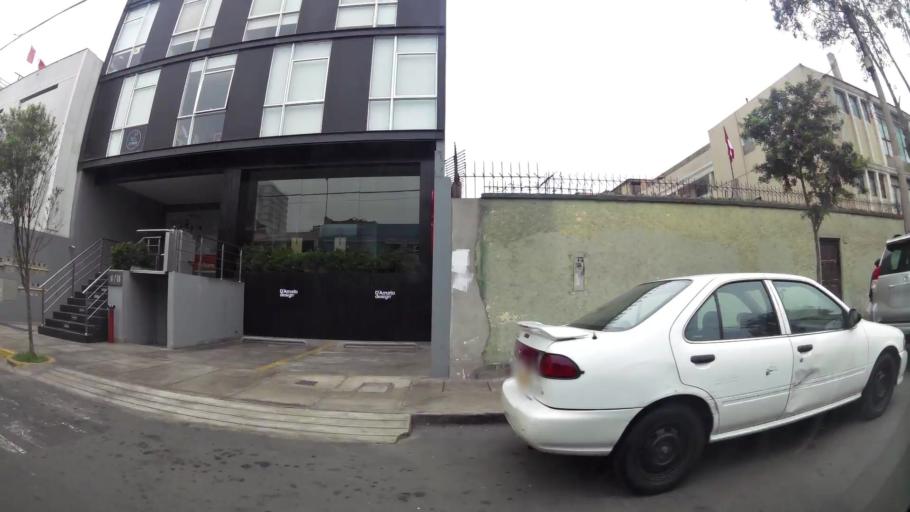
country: PE
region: Lima
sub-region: Lima
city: San Isidro
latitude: -12.1128
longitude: -77.0474
